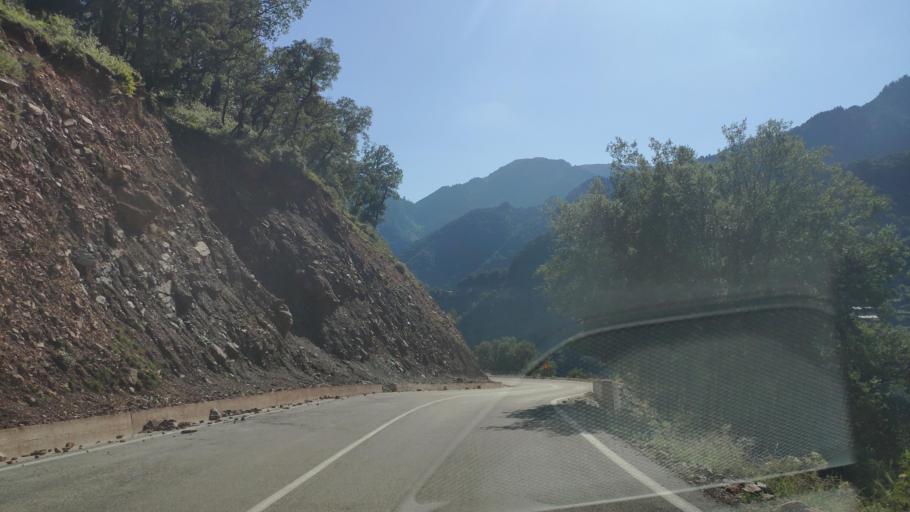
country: GR
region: Central Greece
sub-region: Nomos Evrytanias
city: Kerasochori
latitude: 39.0963
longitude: 21.6081
